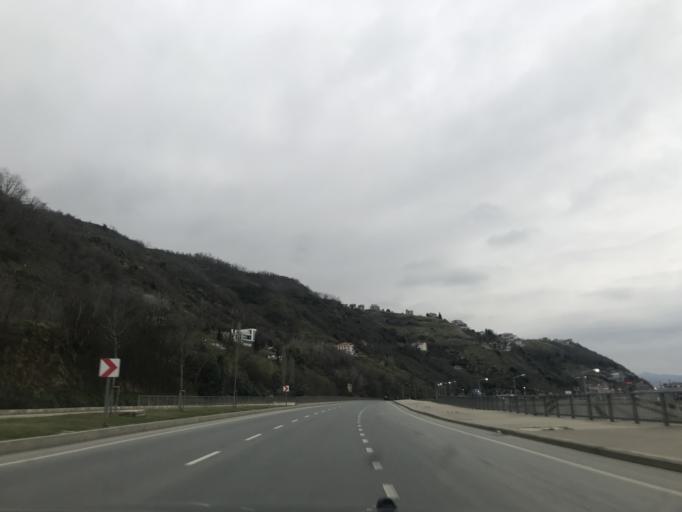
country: TR
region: Trabzon
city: Derecik
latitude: 40.9954
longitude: 39.6505
